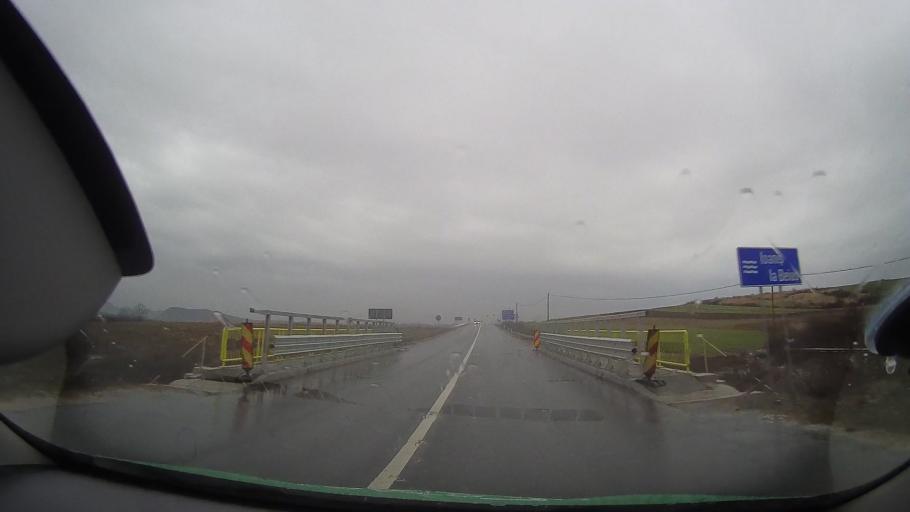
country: RO
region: Bihor
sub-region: Comuna Pocola
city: Pocola
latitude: 46.6812
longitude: 22.3111
